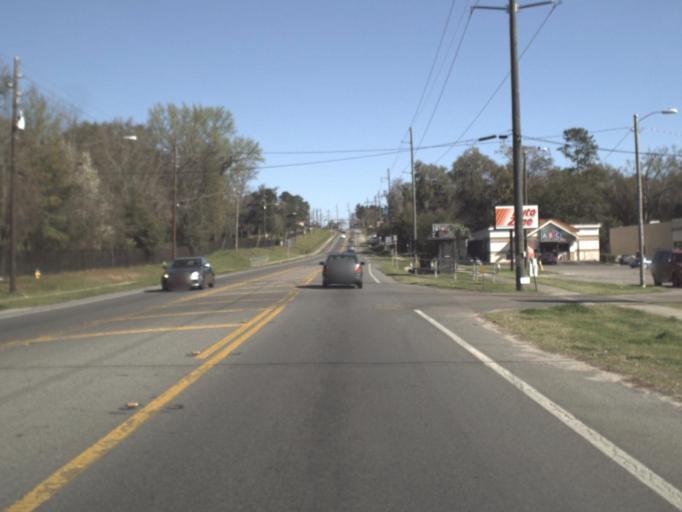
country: US
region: Florida
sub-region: Leon County
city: Tallahassee
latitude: 30.4146
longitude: -84.2827
